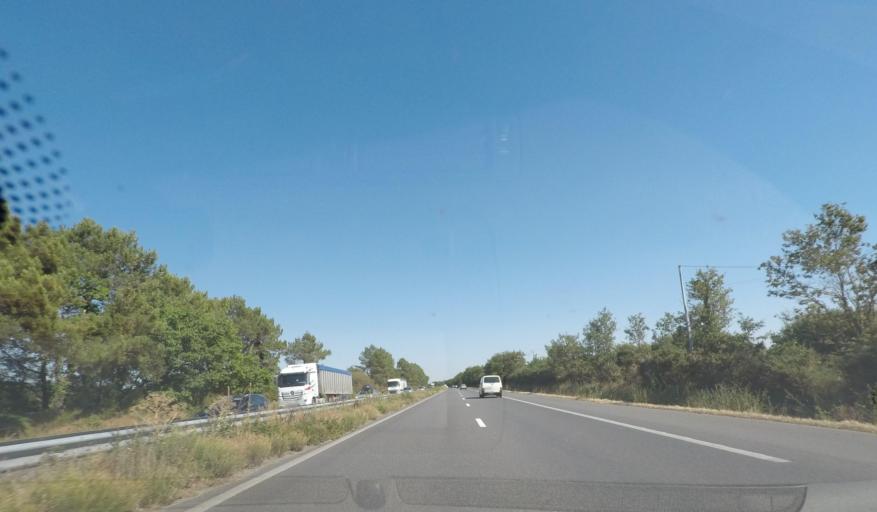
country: FR
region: Pays de la Loire
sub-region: Departement de la Loire-Atlantique
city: La Chapelle-des-Marais
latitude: 47.4911
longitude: -2.2364
